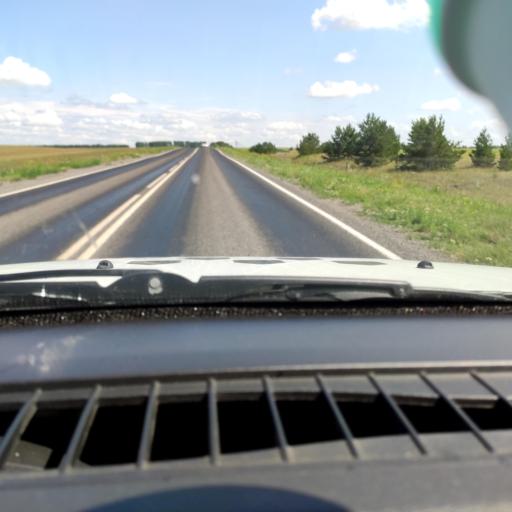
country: RU
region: Bashkortostan
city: Verkhniye Kigi
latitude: 55.4585
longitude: 58.4255
